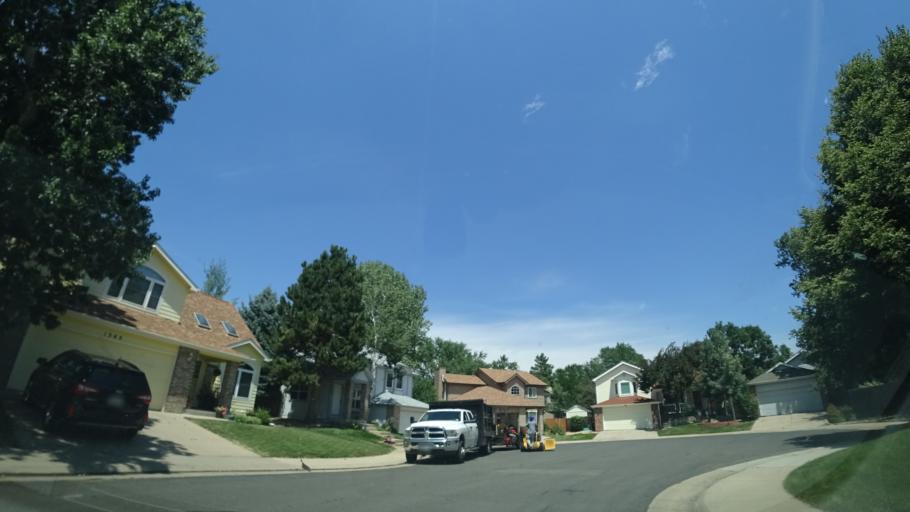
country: US
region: Colorado
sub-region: Jefferson County
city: Lakewood
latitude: 39.6919
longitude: -105.0985
